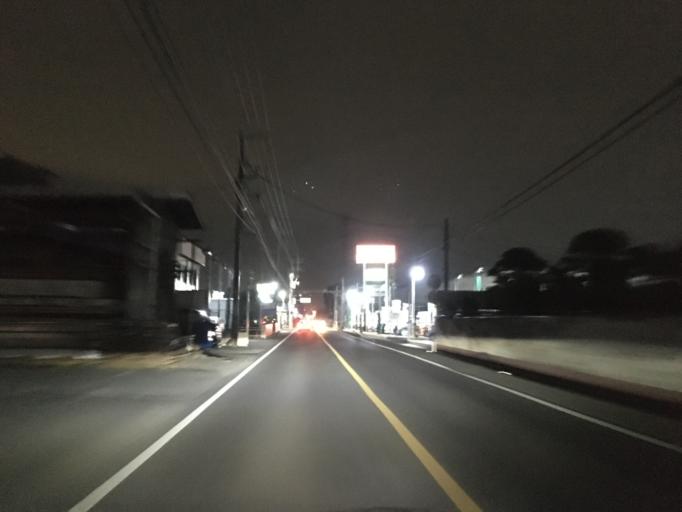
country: JP
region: Saitama
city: Sayama
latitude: 35.8250
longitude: 139.4372
